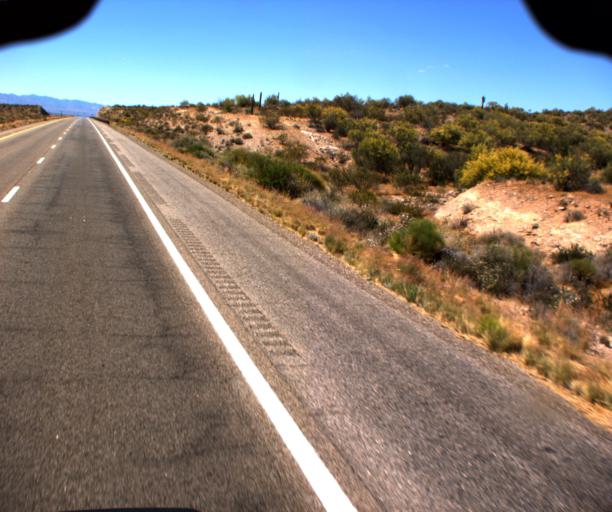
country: US
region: Arizona
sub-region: Yavapai County
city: Bagdad
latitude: 34.5879
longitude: -113.5083
